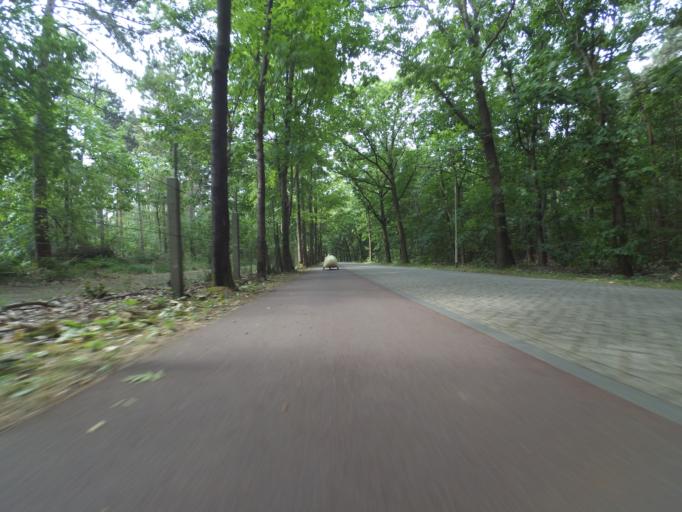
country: NL
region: North Brabant
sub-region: Gemeente Rucphen
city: Rucphen
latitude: 51.5660
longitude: 4.5572
